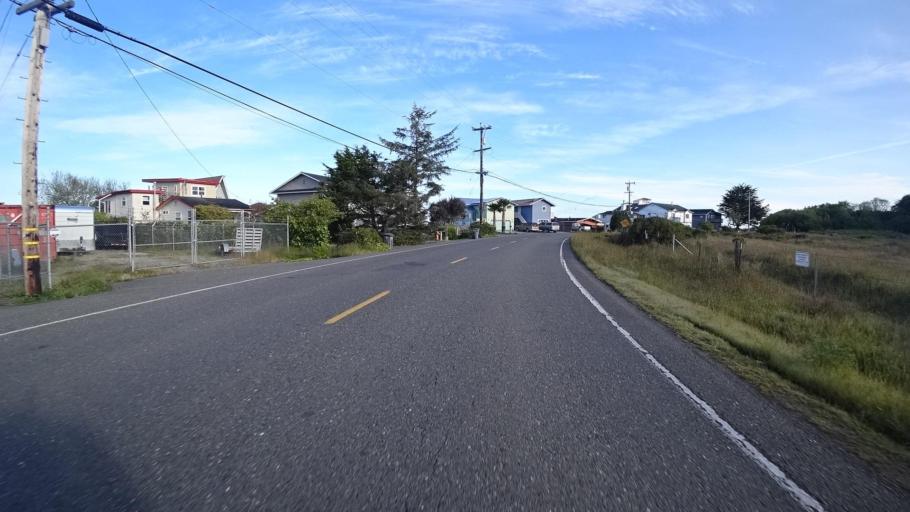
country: US
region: California
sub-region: Humboldt County
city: Humboldt Hill
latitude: 40.7404
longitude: -124.2151
